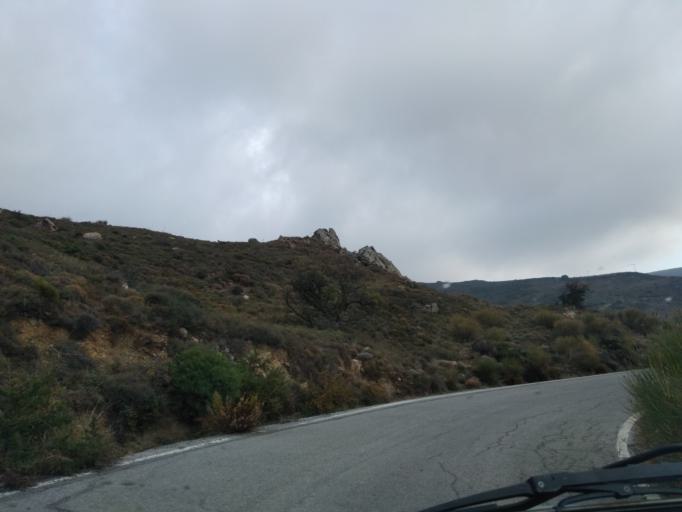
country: GR
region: Crete
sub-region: Nomos Lasithiou
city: Siteia
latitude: 35.1453
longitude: 26.0220
